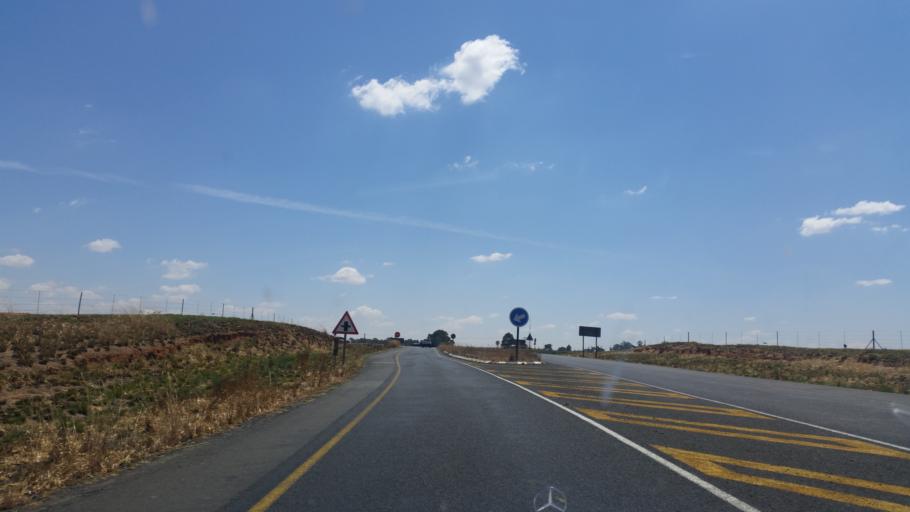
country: ZA
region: Orange Free State
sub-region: Thabo Mofutsanyana District Municipality
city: Reitz
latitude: -28.0845
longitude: 28.6505
